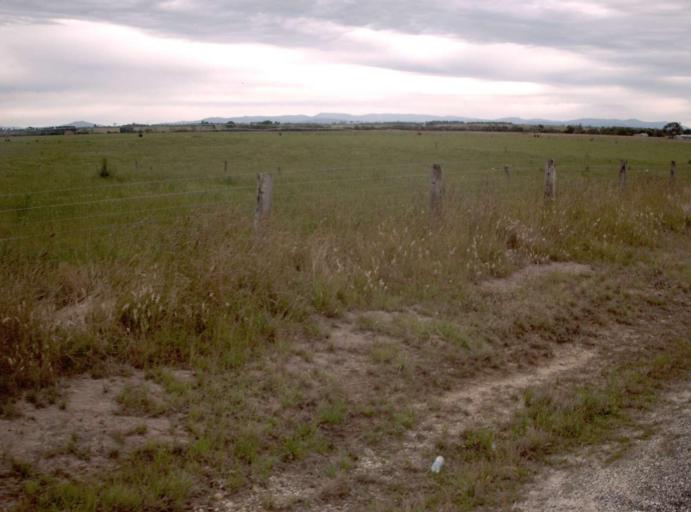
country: AU
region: Victoria
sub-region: Wellington
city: Sale
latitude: -38.0365
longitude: 147.1771
